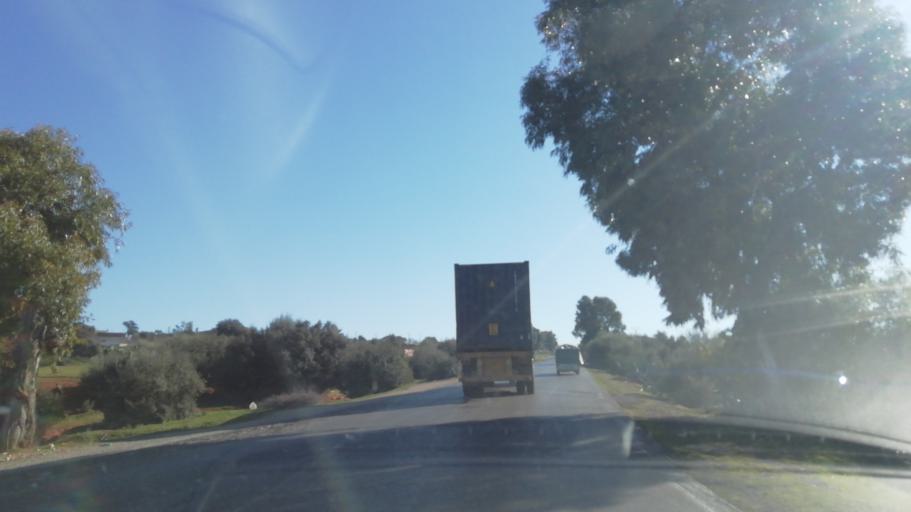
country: DZ
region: Relizane
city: Smala
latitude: 35.6845
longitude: 0.7995
